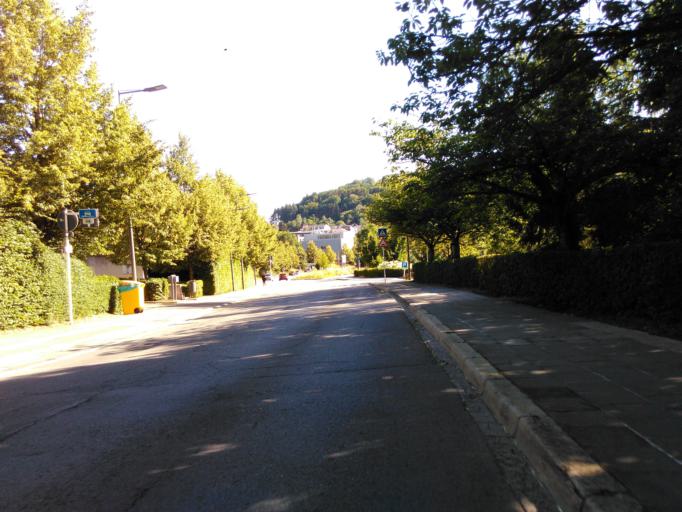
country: LU
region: Luxembourg
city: Belvaux
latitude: 49.5189
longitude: 5.9281
